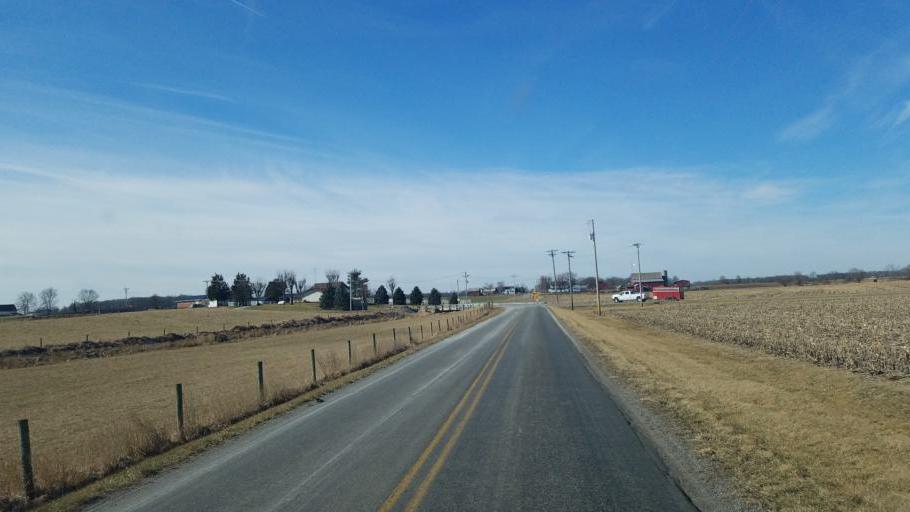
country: US
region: Ohio
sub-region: Hardin County
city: Kenton
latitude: 40.5909
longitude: -83.4482
